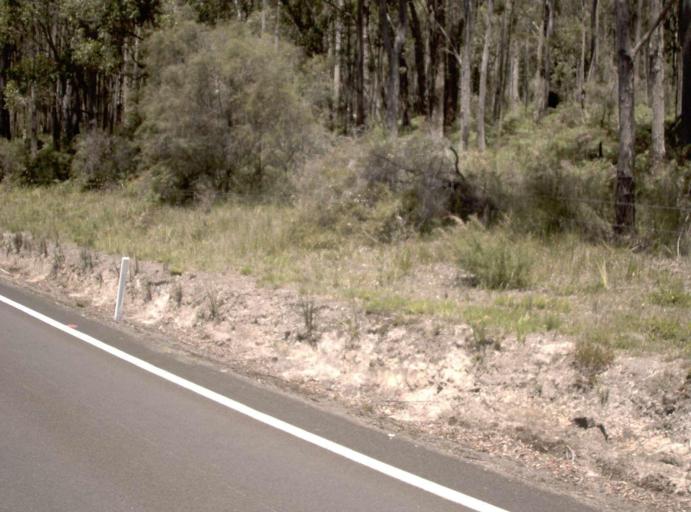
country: AU
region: Victoria
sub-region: East Gippsland
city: Lakes Entrance
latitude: -37.7106
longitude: 148.6778
